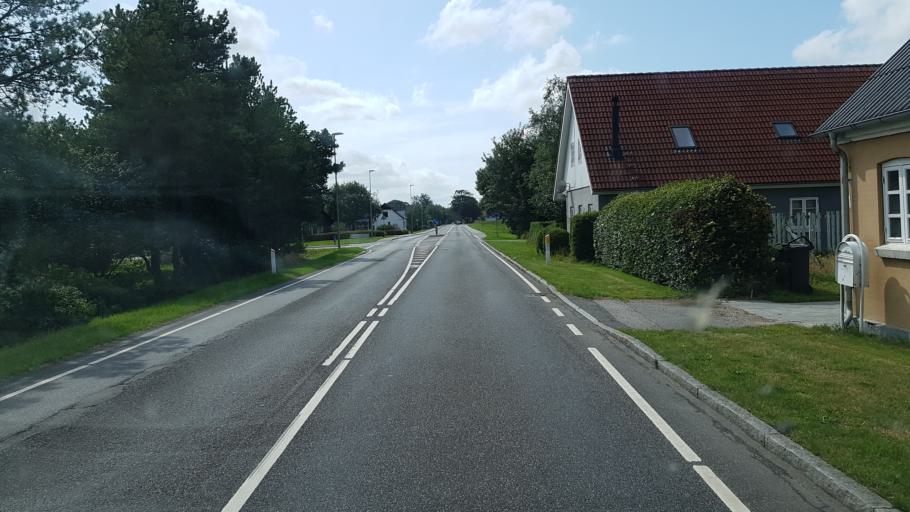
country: DK
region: South Denmark
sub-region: Vejen Kommune
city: Vejen
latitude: 55.5743
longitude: 9.1528
